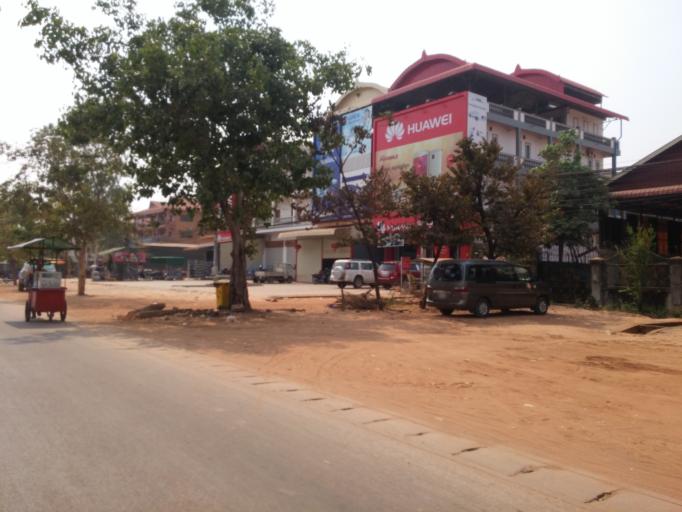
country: KH
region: Siem Reap
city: Siem Reap
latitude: 13.3589
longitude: 103.8839
